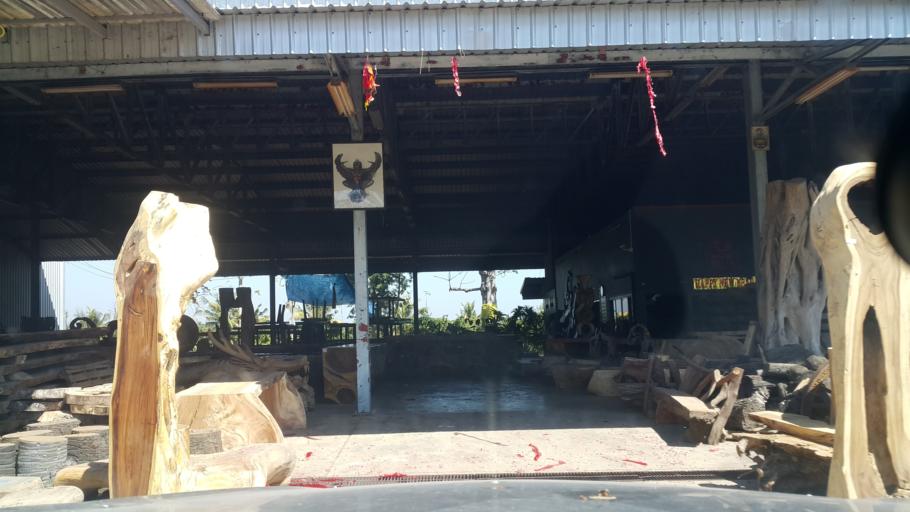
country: TH
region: Chiang Mai
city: Hang Dong
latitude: 18.6823
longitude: 98.9793
